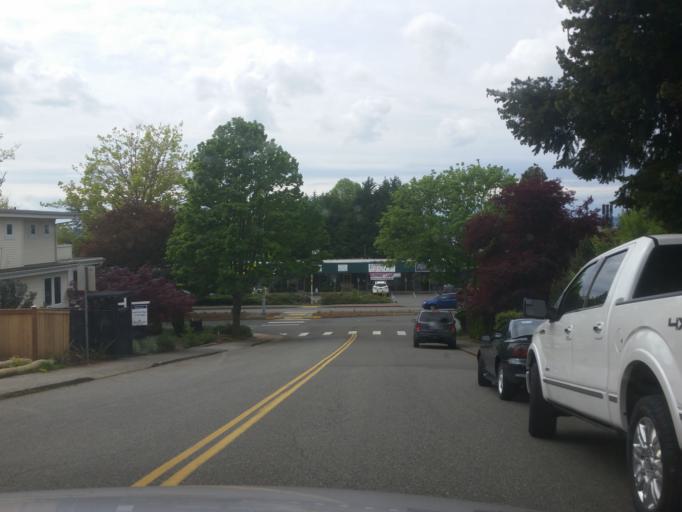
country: US
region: Washington
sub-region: King County
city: Kirkland
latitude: 47.6874
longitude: -122.2089
